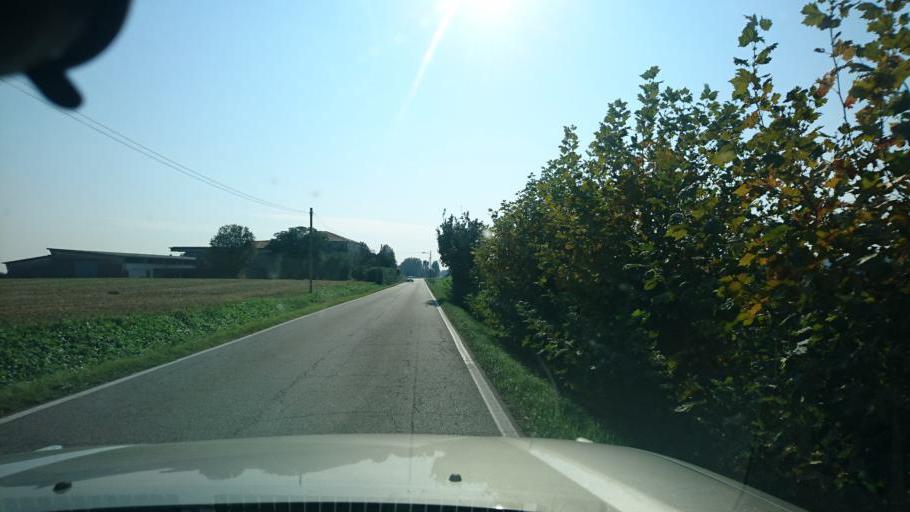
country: IT
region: Veneto
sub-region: Provincia di Vicenza
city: Longare
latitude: 45.4910
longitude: 11.6051
